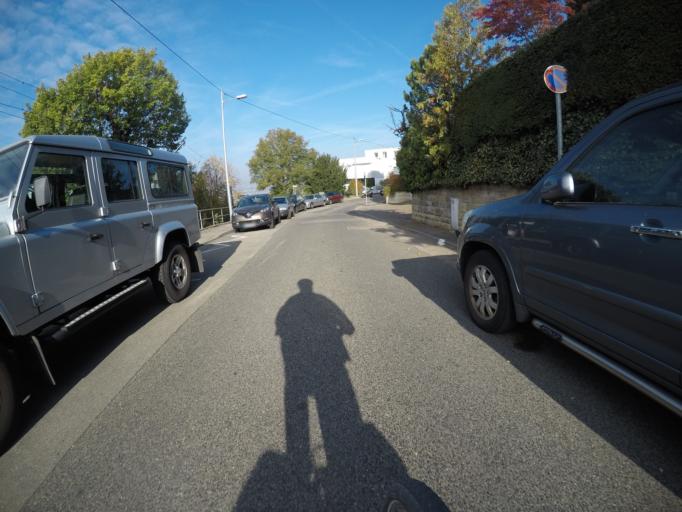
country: DE
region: Baden-Wuerttemberg
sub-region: Regierungsbezirk Stuttgart
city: Stuttgart
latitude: 48.7521
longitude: 9.1733
